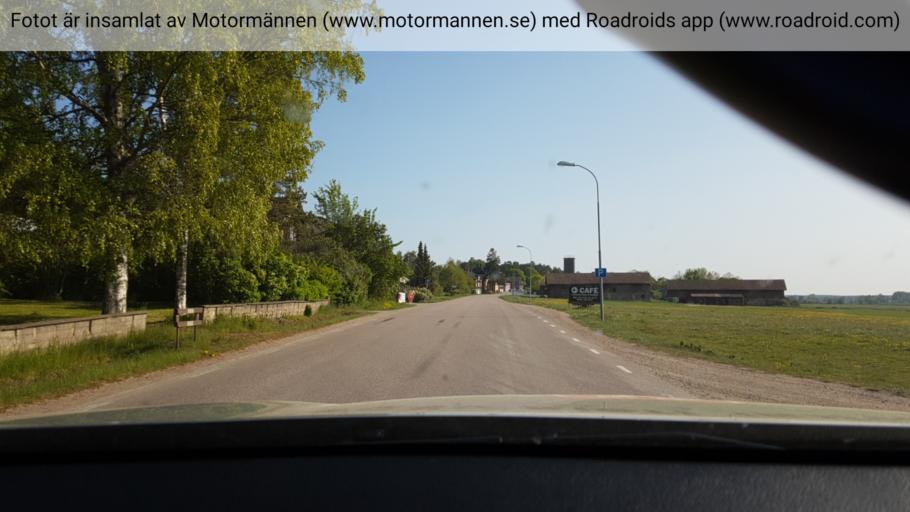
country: SE
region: Uppsala
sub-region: Heby Kommun
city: Tarnsjo
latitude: 60.3144
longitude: 16.7991
